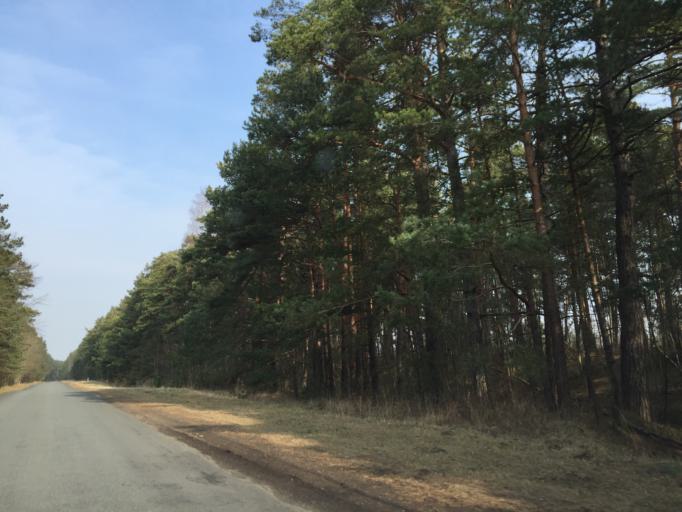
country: LV
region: Salacgrivas
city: Ainazi
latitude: 57.8837
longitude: 24.3663
